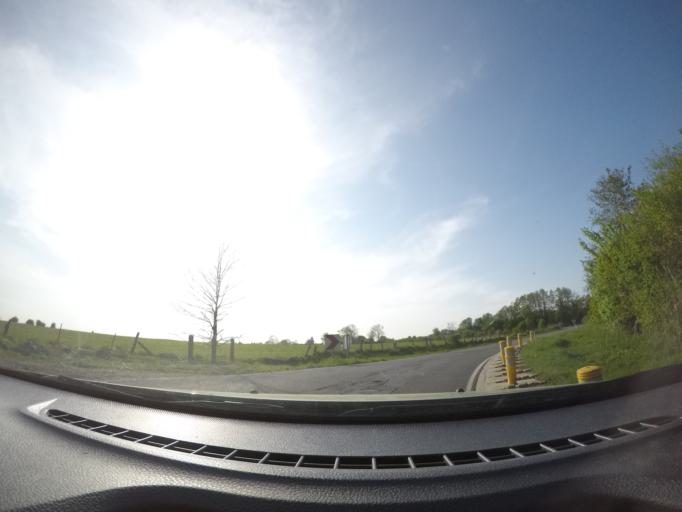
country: BE
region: Wallonia
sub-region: Province du Luxembourg
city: Tintigny
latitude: 49.6631
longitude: 5.5075
